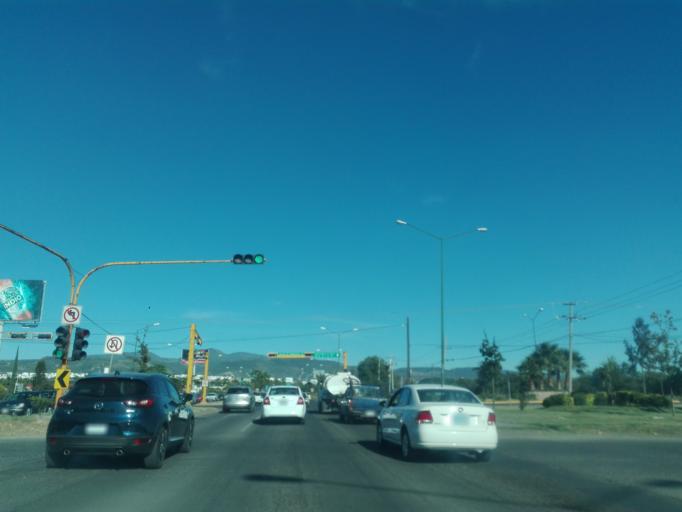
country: MX
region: Guanajuato
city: Leon
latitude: 21.1699
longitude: -101.6865
